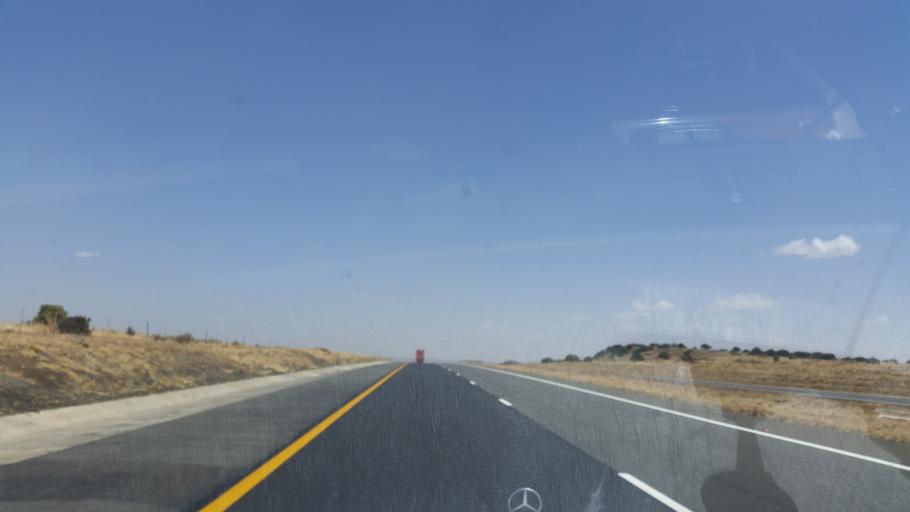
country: ZA
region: Orange Free State
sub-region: Lejweleputswa District Municipality
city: Brandfort
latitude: -28.9164
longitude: 26.4476
